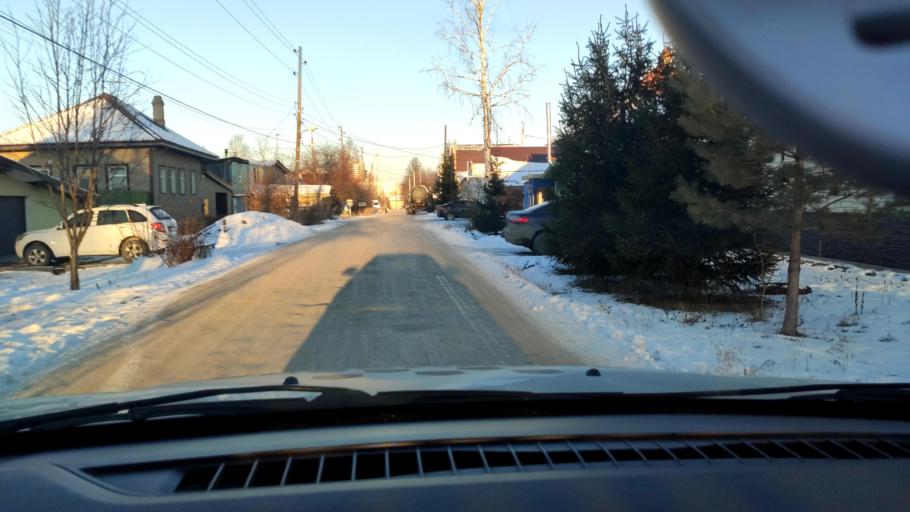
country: RU
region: Perm
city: Perm
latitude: 58.0514
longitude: 56.3356
